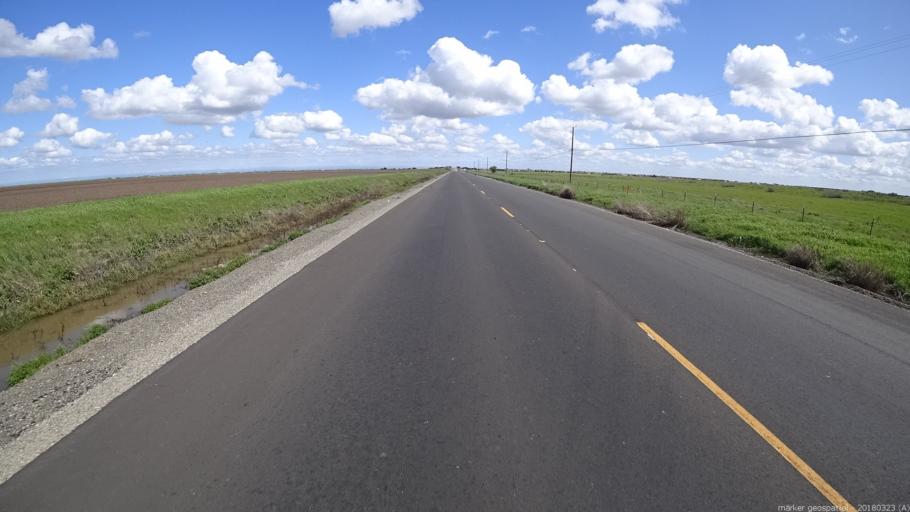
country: US
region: California
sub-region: Sacramento County
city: Elverta
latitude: 38.6856
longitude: -121.5546
